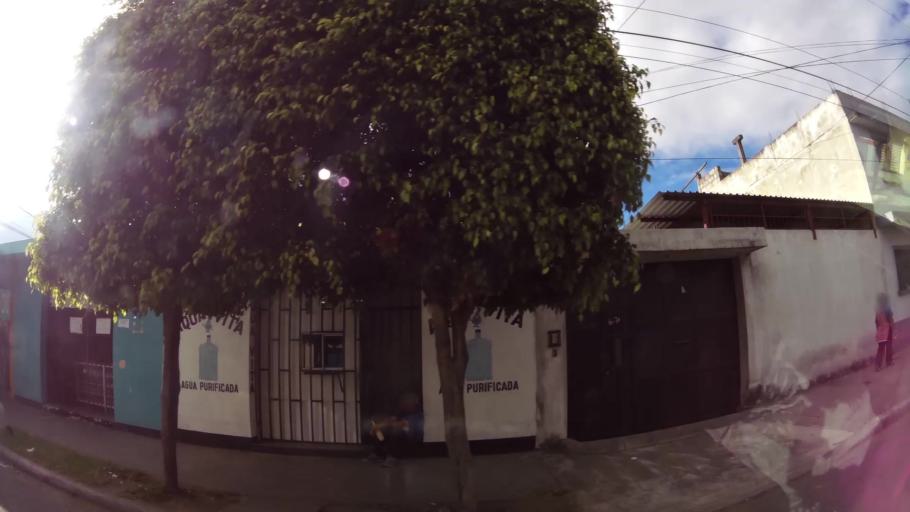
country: GT
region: Guatemala
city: Guatemala City
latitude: 14.6166
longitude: -90.5486
